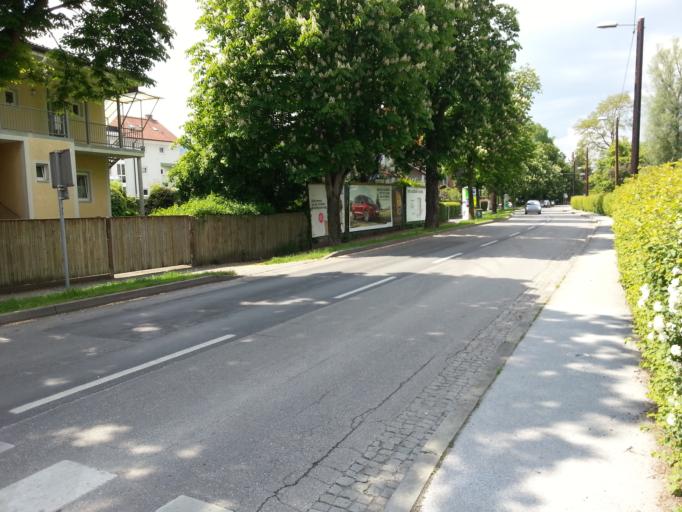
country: AT
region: Styria
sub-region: Graz Stadt
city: Graz
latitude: 47.0826
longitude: 15.4268
